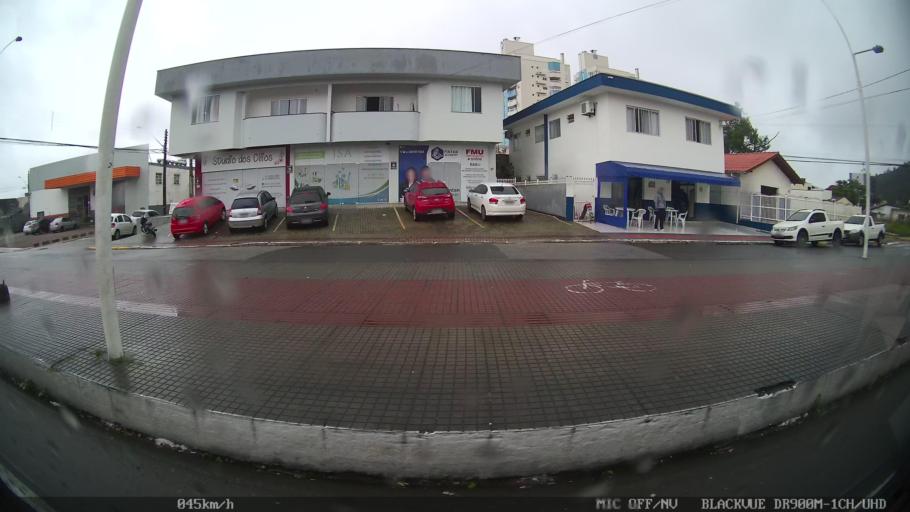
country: BR
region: Santa Catarina
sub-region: Itajai
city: Itajai
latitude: -26.9196
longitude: -48.6733
